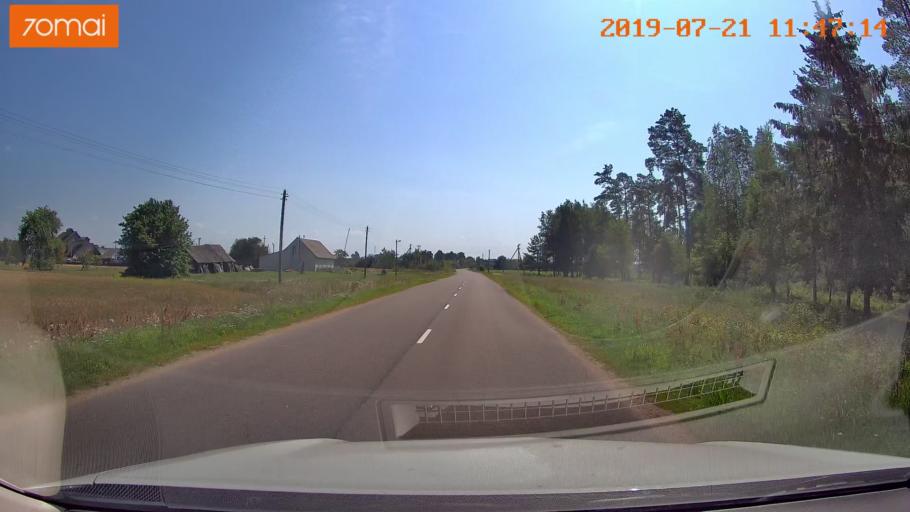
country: BY
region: Grodnenskaya
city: Lyubcha
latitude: 53.9037
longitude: 26.0437
